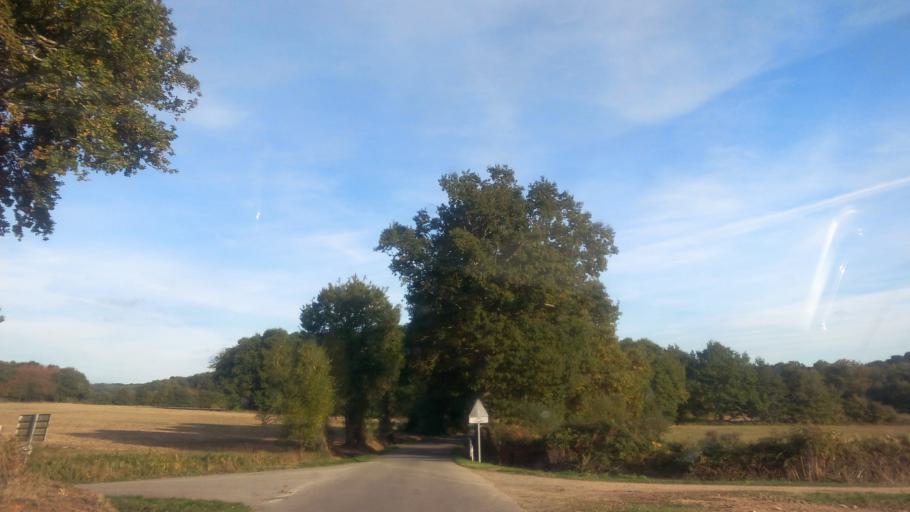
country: FR
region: Brittany
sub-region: Departement du Morbihan
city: Saint-Perreux
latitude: 47.6892
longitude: -2.1041
